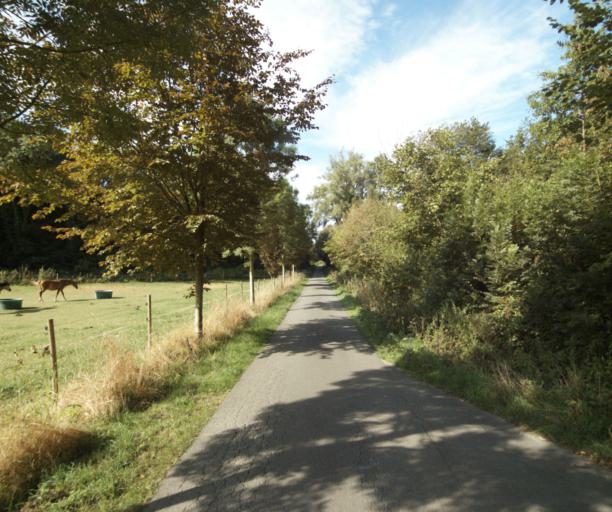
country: FR
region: Nord-Pas-de-Calais
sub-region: Departement du Nord
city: Sainghin-en-Melantois
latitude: 50.5857
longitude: 3.1801
